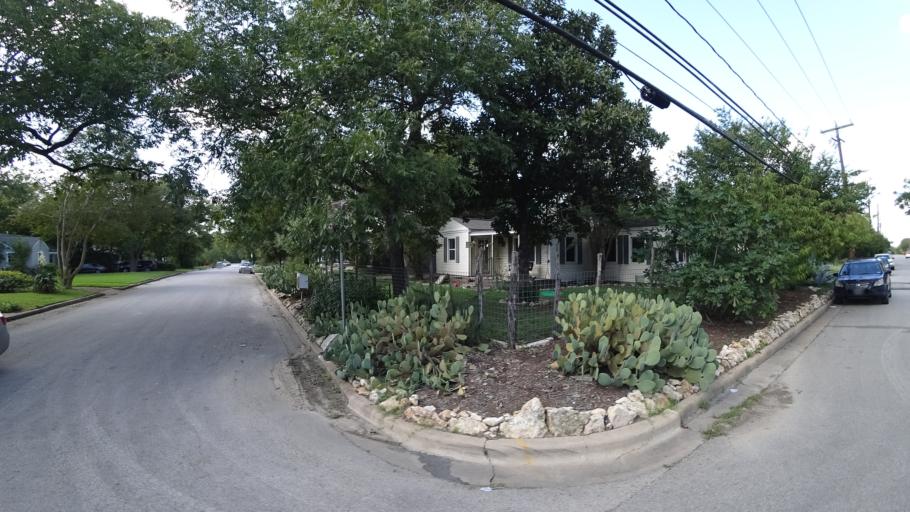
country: US
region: Texas
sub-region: Travis County
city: Austin
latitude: 30.3082
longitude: -97.7134
